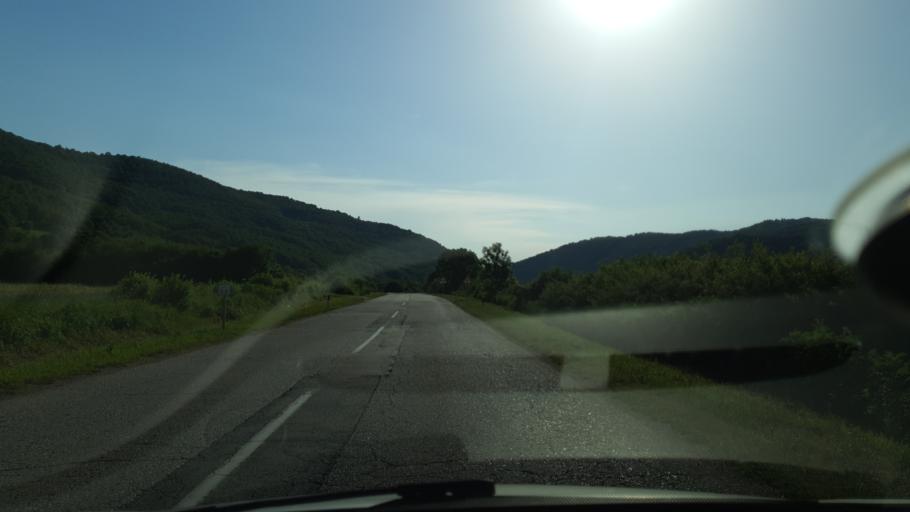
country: RS
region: Central Serbia
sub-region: Zajecarski Okrug
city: Soko Banja
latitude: 43.6535
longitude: 21.7710
